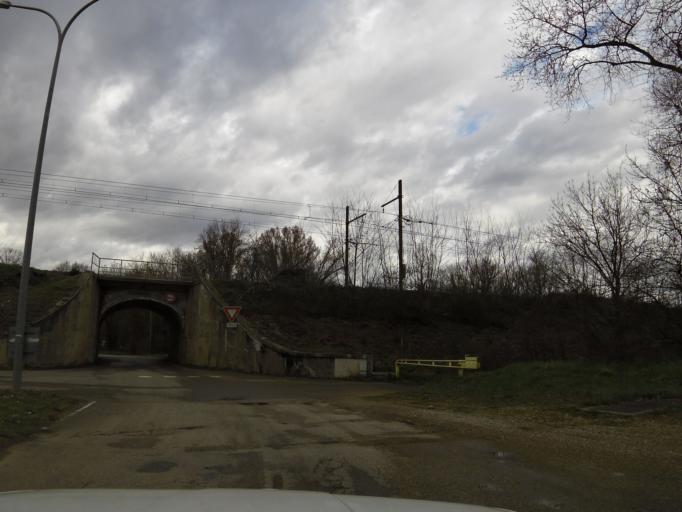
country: FR
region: Rhone-Alpes
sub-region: Departement de l'Ain
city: Chazey-sur-Ain
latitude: 45.9178
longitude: 5.2367
